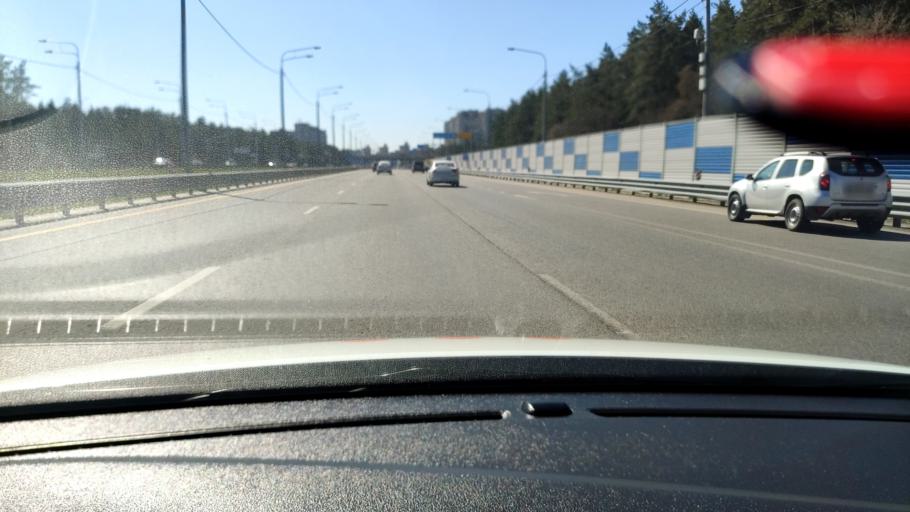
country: RU
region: Voronezj
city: Podgornoye
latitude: 51.7392
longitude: 39.1830
